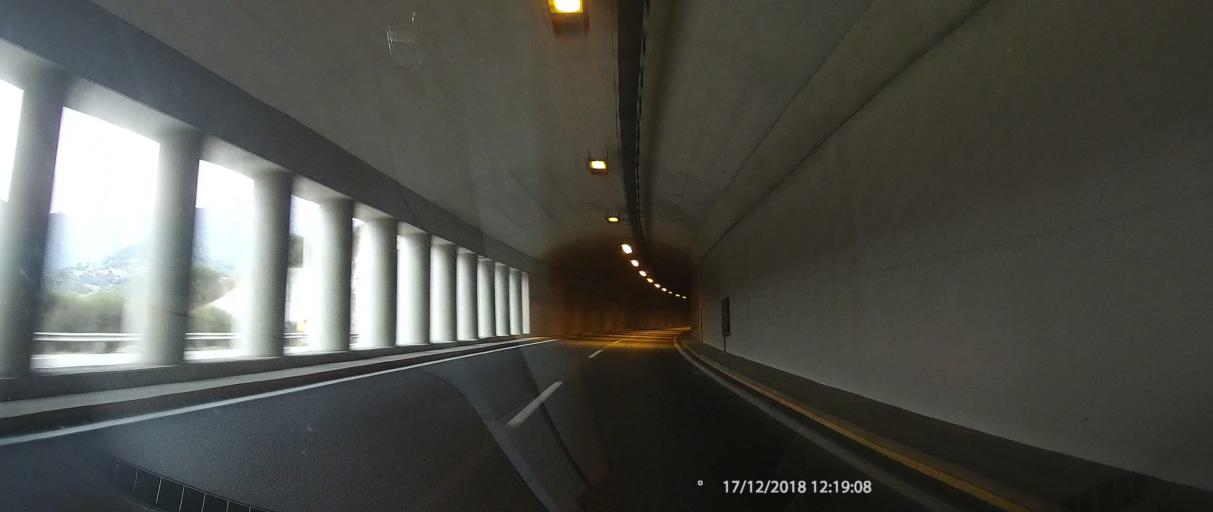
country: GR
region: Epirus
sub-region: Nomos Ioanninon
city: Metsovo
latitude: 39.7620
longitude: 21.0966
